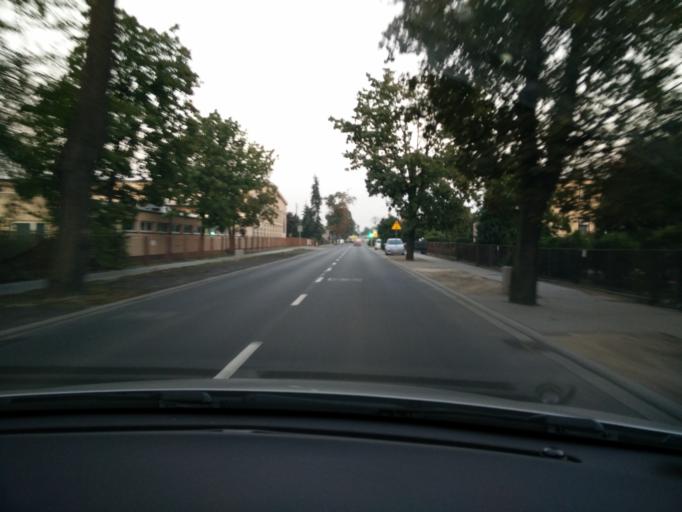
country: PL
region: Greater Poland Voivodeship
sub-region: Powiat sredzki
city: Sroda Wielkopolska
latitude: 52.2321
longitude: 17.2612
